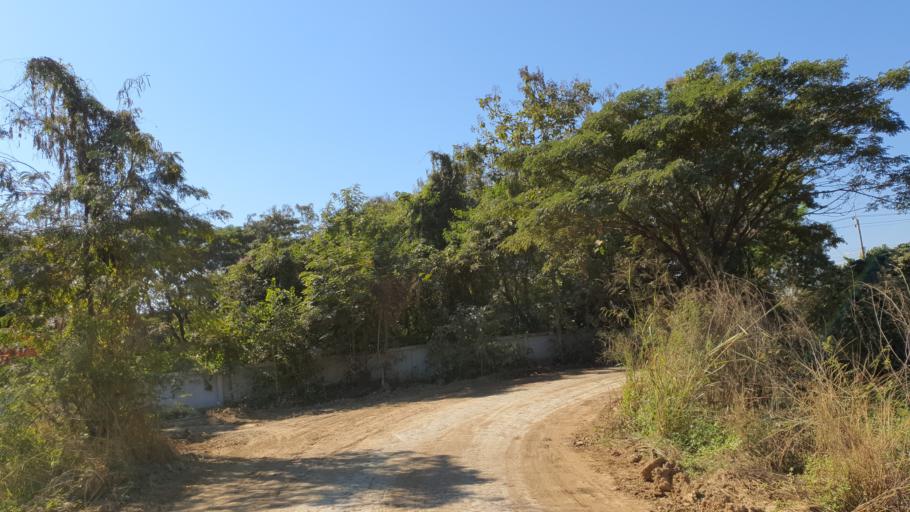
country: TH
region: Lamphun
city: Ban Thi
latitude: 18.6634
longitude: 99.1051
